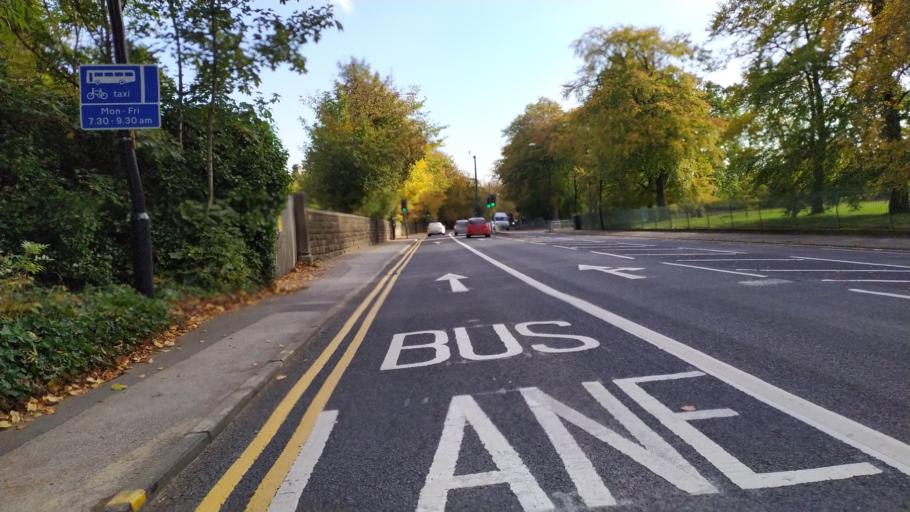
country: GB
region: England
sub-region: City and Borough of Leeds
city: Chapel Allerton
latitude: 53.8318
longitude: -1.5890
